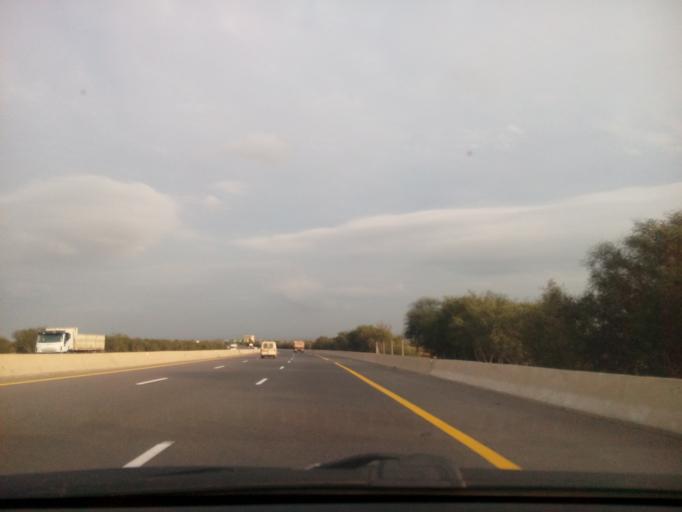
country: DZ
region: Relizane
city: Relizane
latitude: 35.7888
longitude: 0.4119
